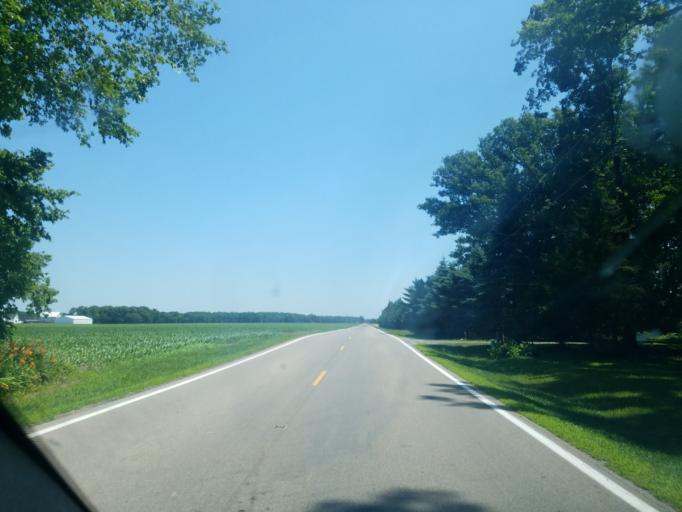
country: US
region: Ohio
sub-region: Allen County
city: Spencerville
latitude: 40.7429
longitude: -84.4342
